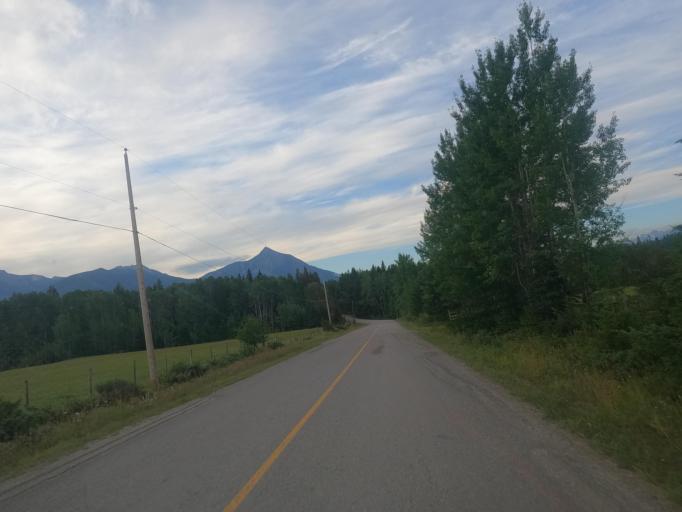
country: CA
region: British Columbia
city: Golden
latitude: 51.4348
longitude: -117.0521
